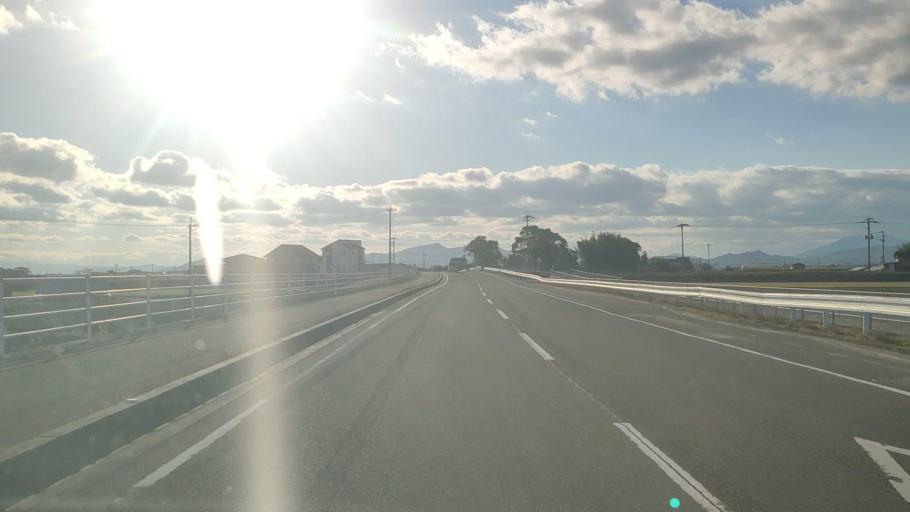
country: JP
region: Saga Prefecture
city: Saga-shi
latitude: 33.2976
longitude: 130.2460
